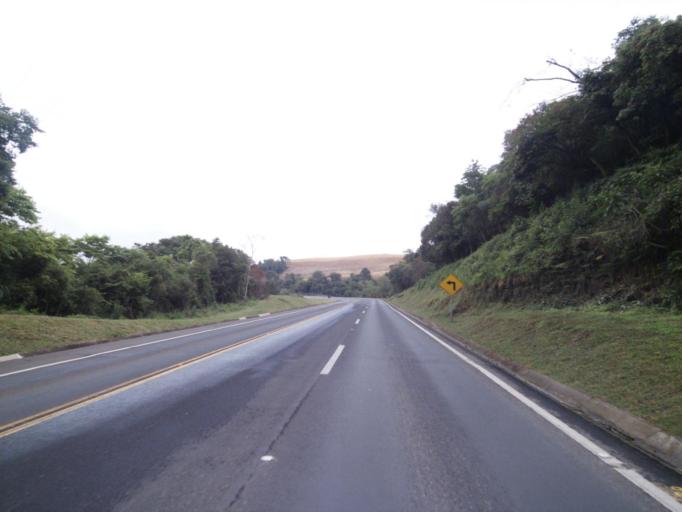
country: BR
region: Parana
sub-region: Irati
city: Irati
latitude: -25.4495
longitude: -50.6374
